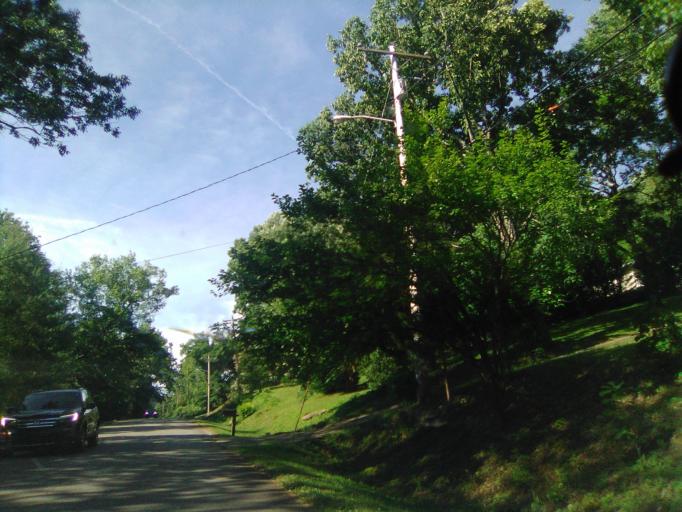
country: US
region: Tennessee
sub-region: Davidson County
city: Belle Meade
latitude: 36.1226
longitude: -86.9057
